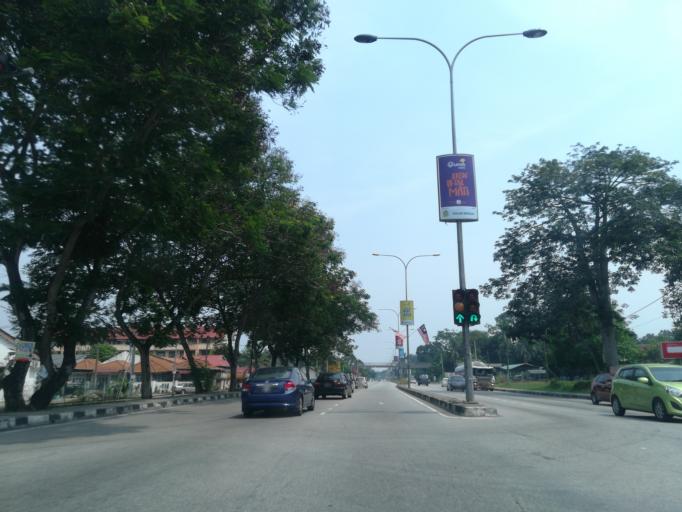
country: MY
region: Kedah
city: Kulim
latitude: 5.4140
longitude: 100.5417
